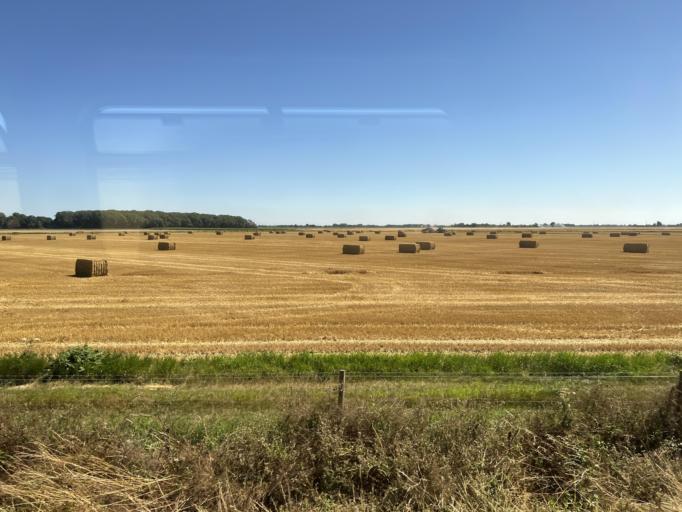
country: GB
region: England
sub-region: Lincolnshire
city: Spilsby
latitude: 53.1066
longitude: 0.1187
